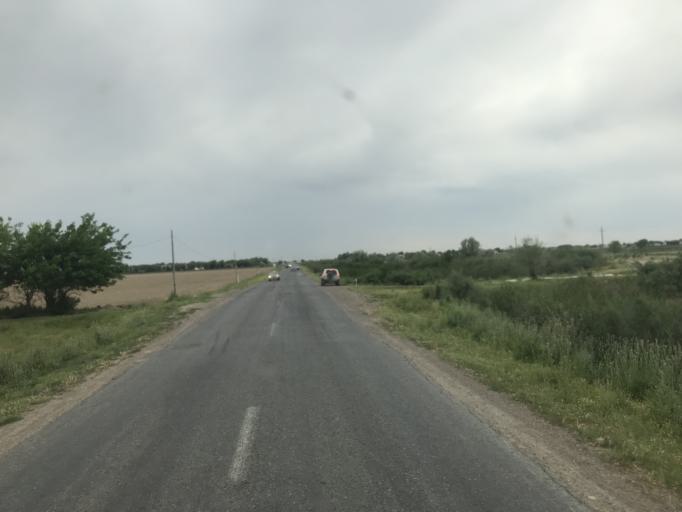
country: KZ
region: Ongtustik Qazaqstan
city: Asykata
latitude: 40.9201
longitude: 68.3994
